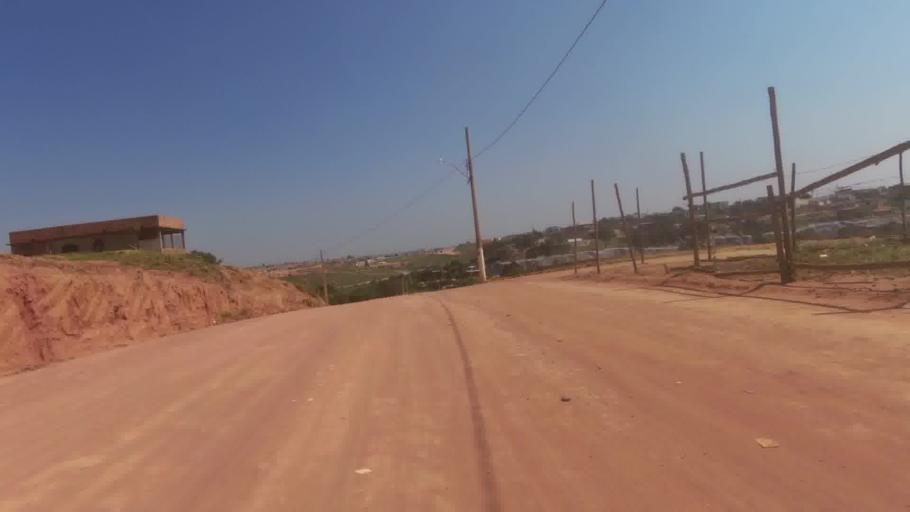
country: BR
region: Espirito Santo
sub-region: Itapemirim
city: Itapemirim
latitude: -21.0175
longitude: -40.8251
